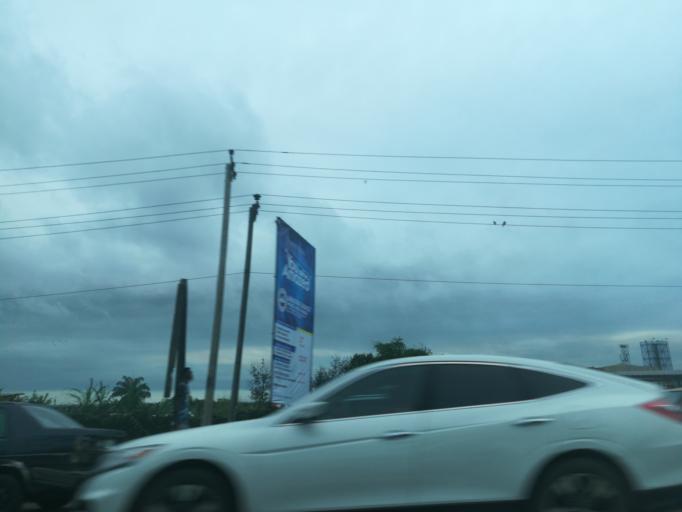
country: NG
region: Rivers
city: Port Harcourt
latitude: 4.8139
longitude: 6.9853
